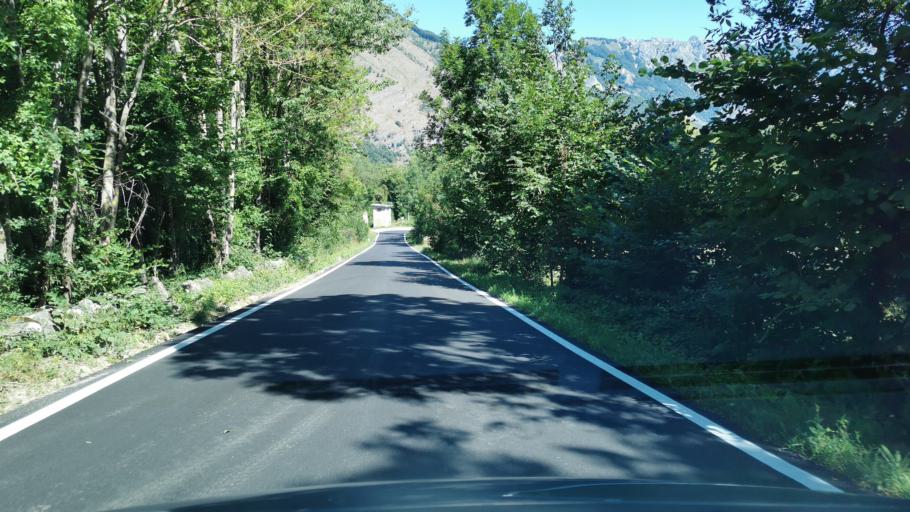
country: IT
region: Piedmont
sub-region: Provincia di Cuneo
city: Entracque
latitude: 44.2518
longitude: 7.3837
